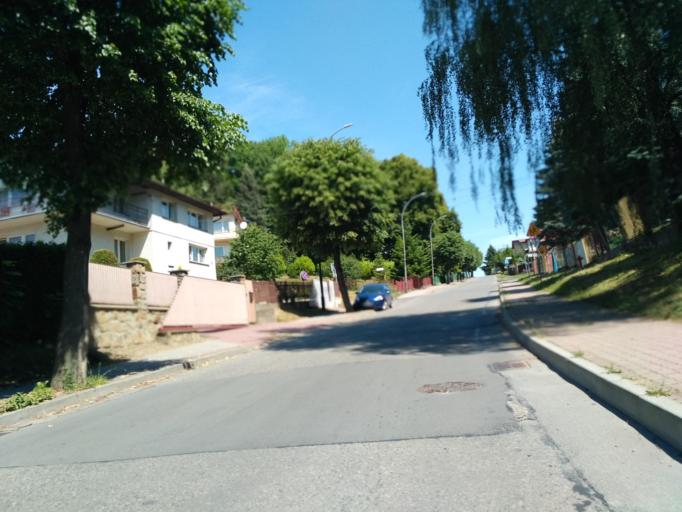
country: PL
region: Subcarpathian Voivodeship
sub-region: Krosno
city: Krosno
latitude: 49.6966
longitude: 21.7751
